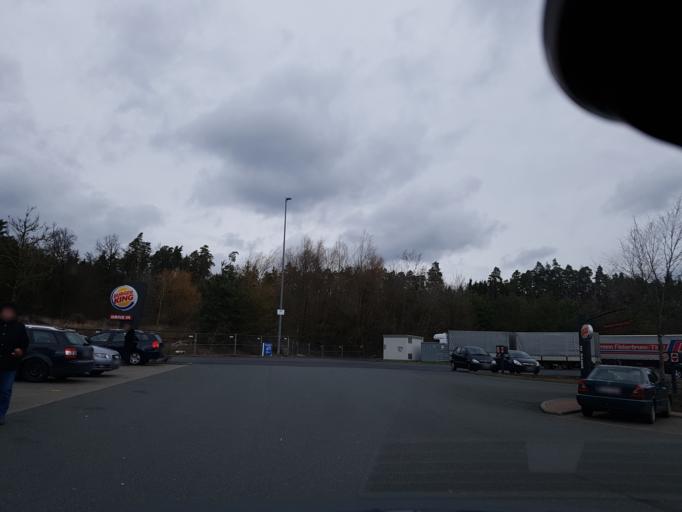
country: DE
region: Bavaria
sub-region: Regierungsbezirk Mittelfranken
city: Schnaittach
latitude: 49.5676
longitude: 11.3271
